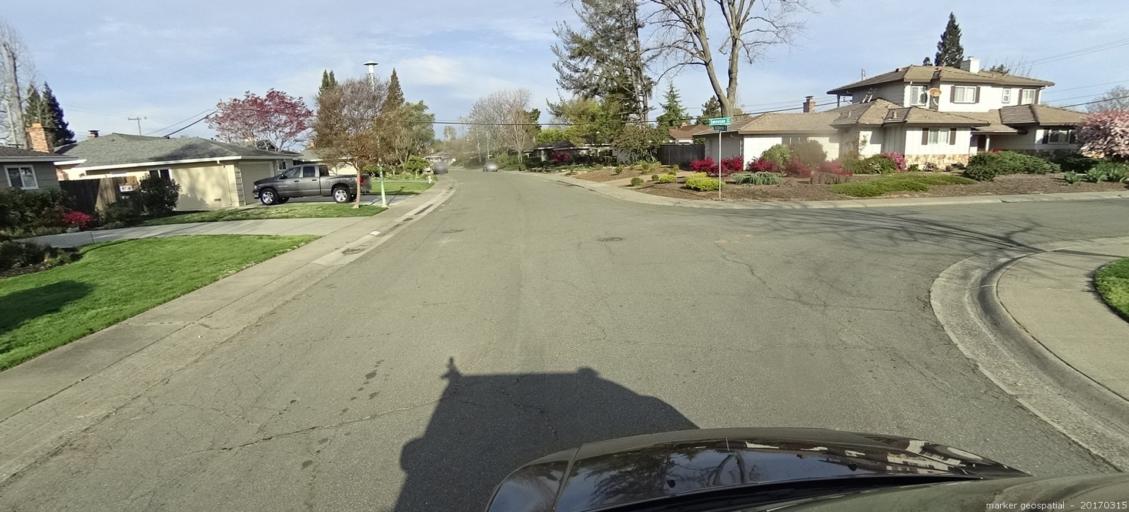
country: US
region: California
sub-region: Sacramento County
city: Parkway
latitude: 38.5024
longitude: -121.5111
